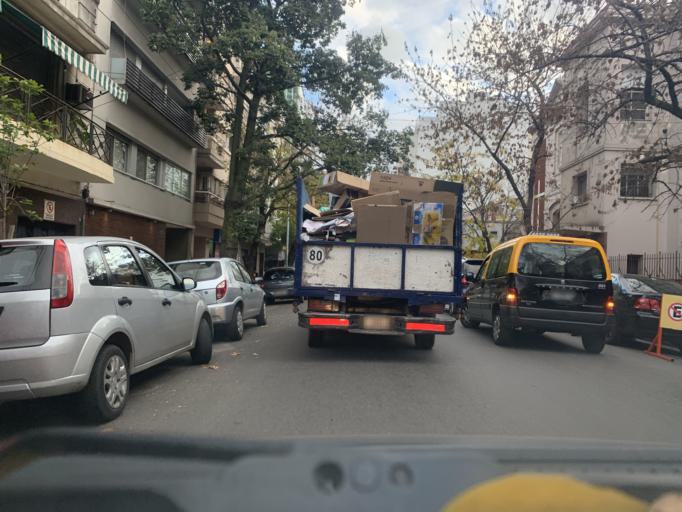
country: AR
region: Buenos Aires F.D.
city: Colegiales
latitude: -34.5781
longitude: -58.4395
